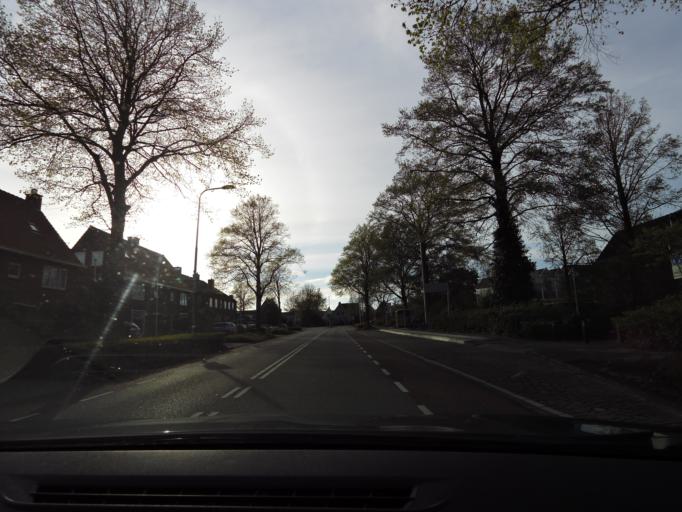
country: NL
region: South Holland
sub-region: Gemeente Lisse
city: Lisse
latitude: 52.2658
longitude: 4.5607
